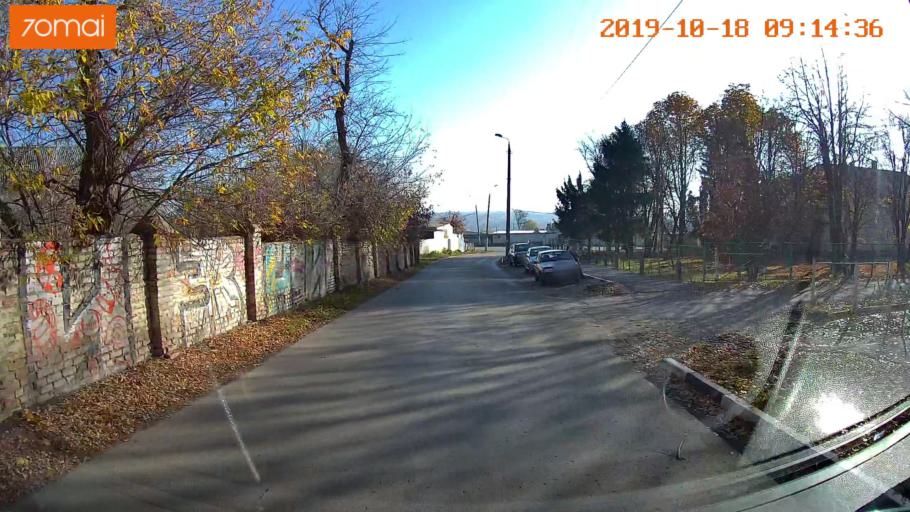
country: RU
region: Tula
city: Yefremov
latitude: 53.1329
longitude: 38.1137
